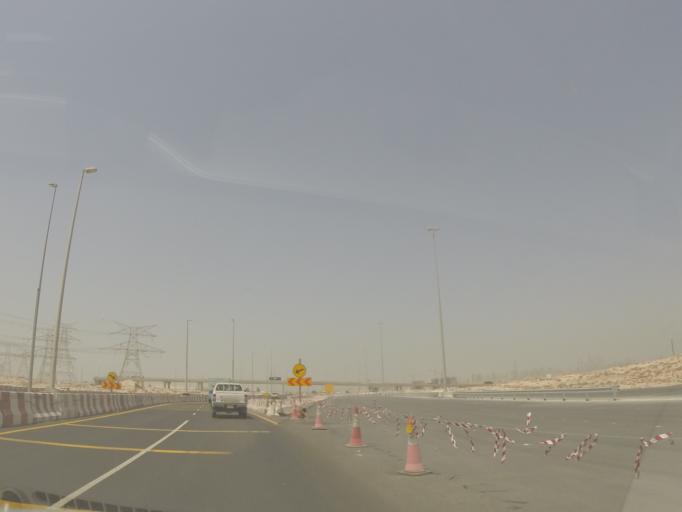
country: AE
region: Dubai
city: Dubai
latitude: 25.0135
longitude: 55.1644
